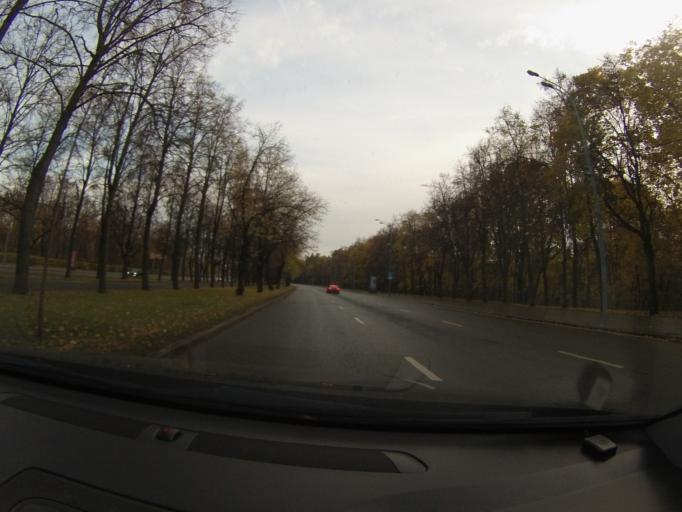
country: RU
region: Moscow
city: Vorob'yovo
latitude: 55.7127
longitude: 37.5372
